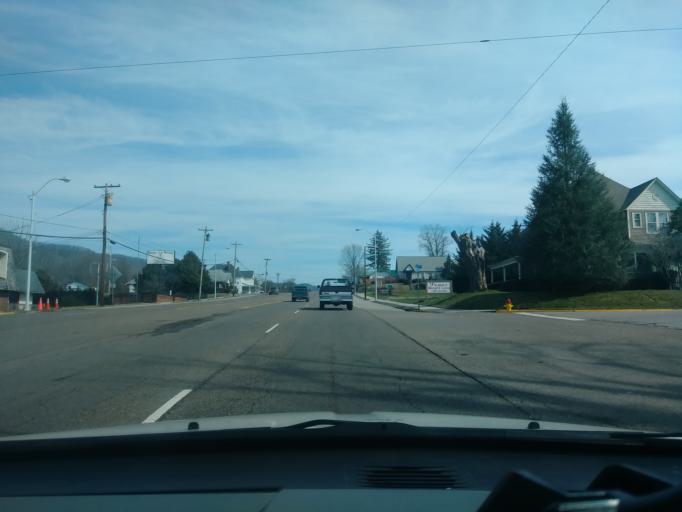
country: US
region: Tennessee
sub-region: Campbell County
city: LaFollette
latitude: 36.3879
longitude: -84.1076
